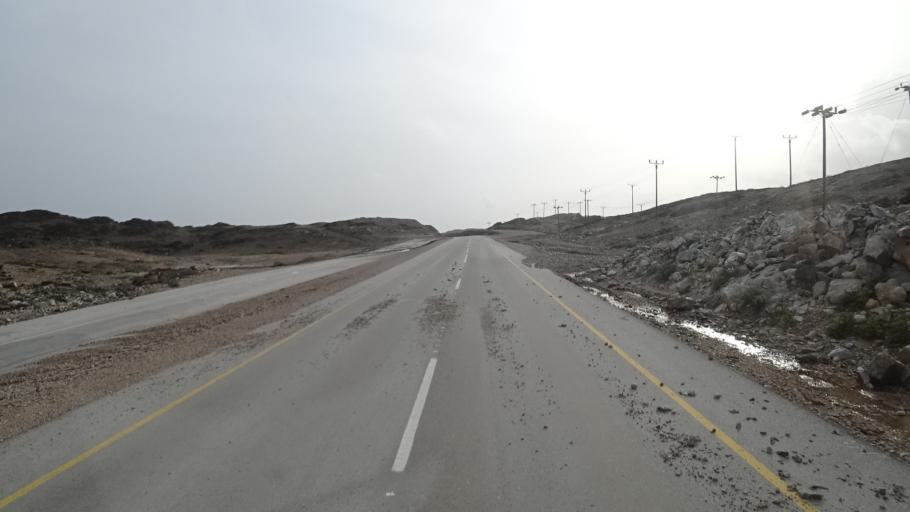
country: OM
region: Zufar
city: Salalah
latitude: 17.0514
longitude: 54.8548
